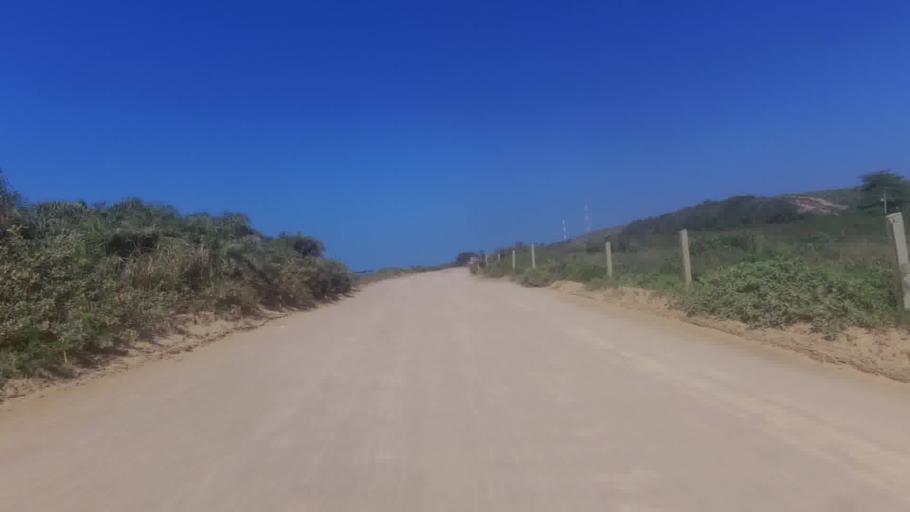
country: BR
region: Espirito Santo
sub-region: Marataizes
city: Marataizes
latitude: -21.0964
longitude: -40.8467
